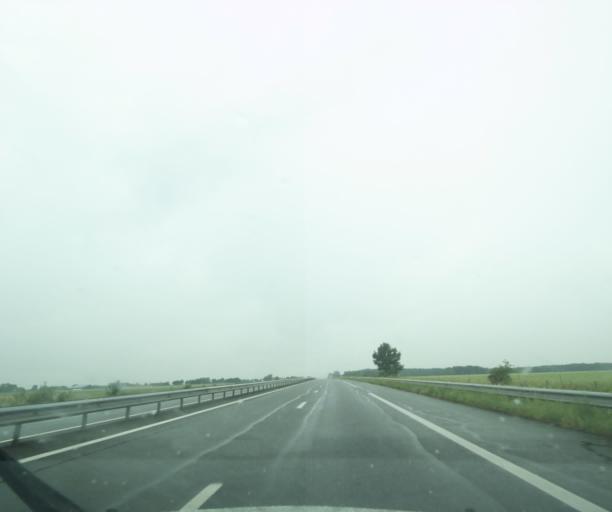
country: FR
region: Auvergne
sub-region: Departement de l'Allier
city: Vallon-en-Sully
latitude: 46.5861
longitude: 2.5222
